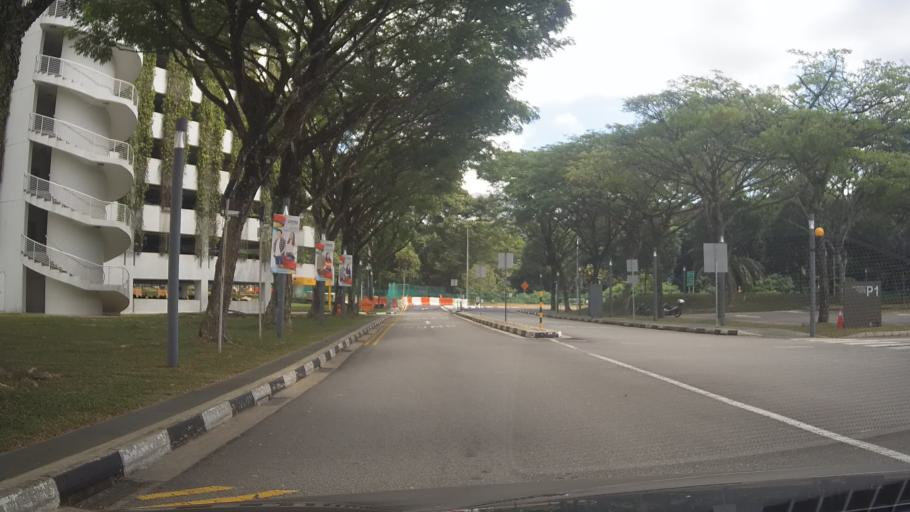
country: MY
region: Johor
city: Johor Bahru
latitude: 1.4444
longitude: 103.7869
